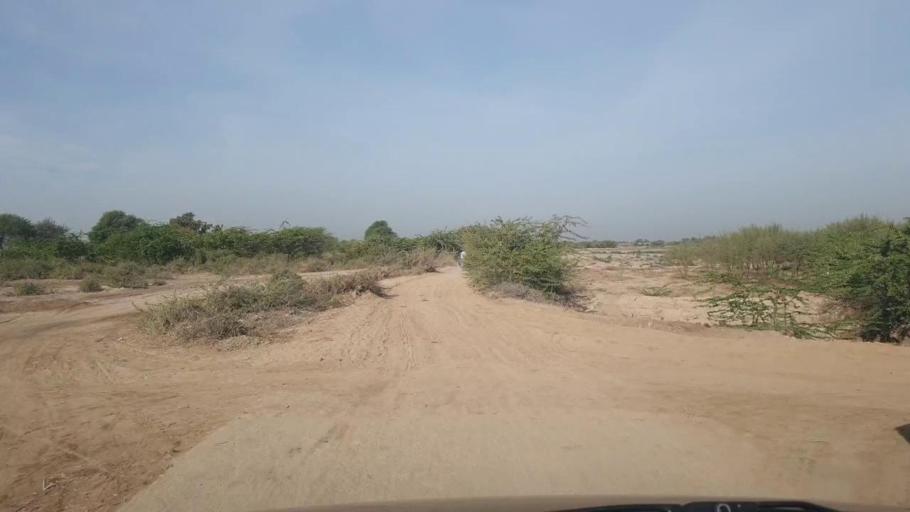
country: PK
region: Sindh
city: Umarkot
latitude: 25.3268
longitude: 69.7031
